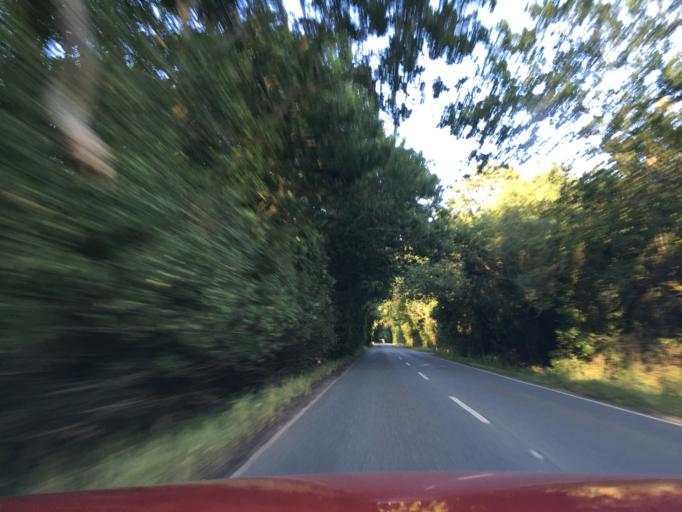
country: GB
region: England
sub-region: Hampshire
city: Tadley
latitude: 51.3611
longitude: -1.1737
